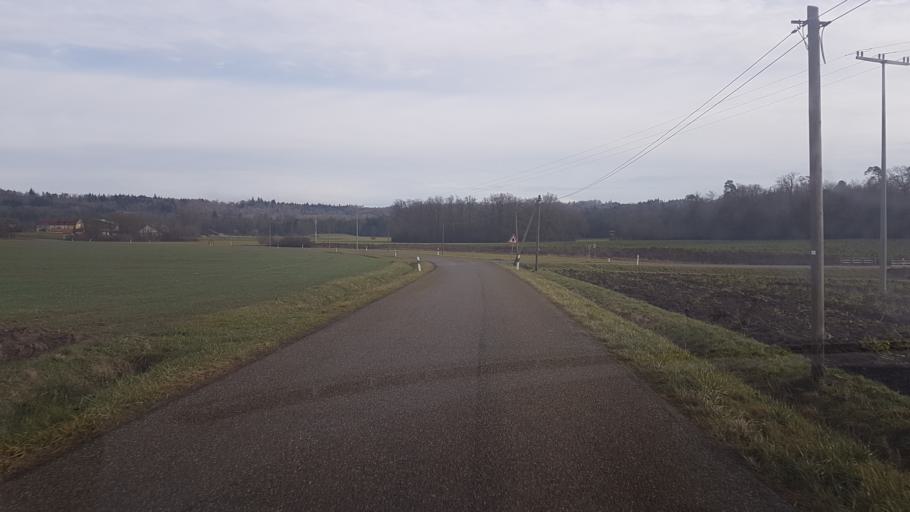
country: DE
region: Bavaria
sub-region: Regierungsbezirk Mittelfranken
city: Wettringen
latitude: 49.2324
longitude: 10.1435
